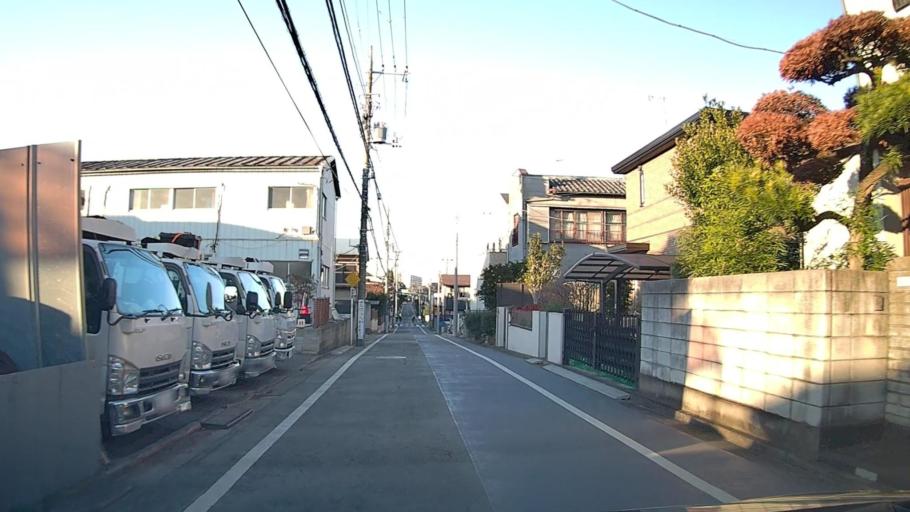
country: JP
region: Saitama
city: Wako
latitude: 35.7610
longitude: 139.6421
